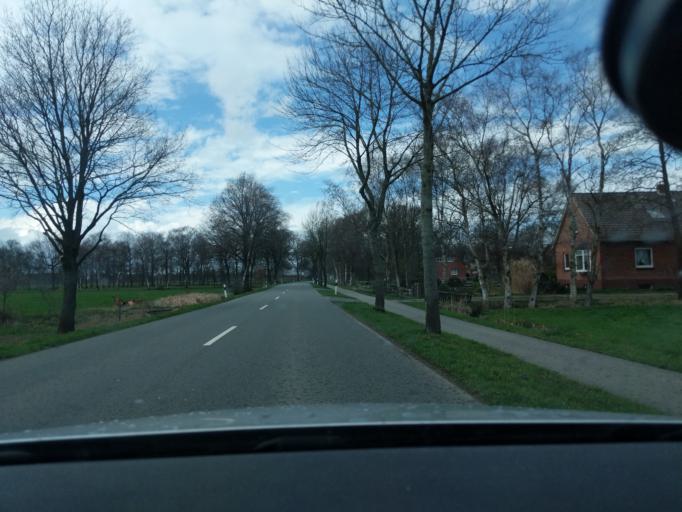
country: DE
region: Lower Saxony
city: Drochtersen
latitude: 53.6705
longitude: 9.3742
